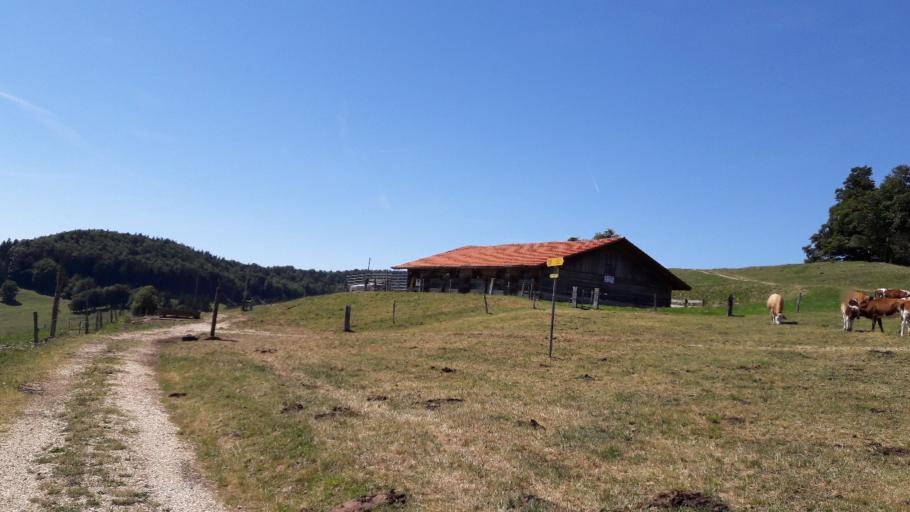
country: CH
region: Solothurn
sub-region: Bezirk Thal
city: Welschenrohr
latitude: 47.3110
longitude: 7.5659
